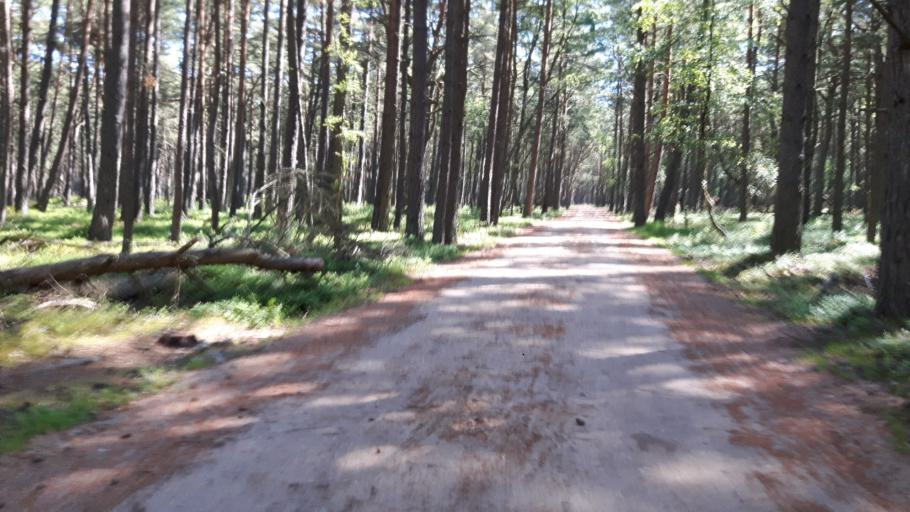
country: PL
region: Pomeranian Voivodeship
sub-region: Powiat slupski
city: Smoldzino
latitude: 54.6732
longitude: 17.1078
